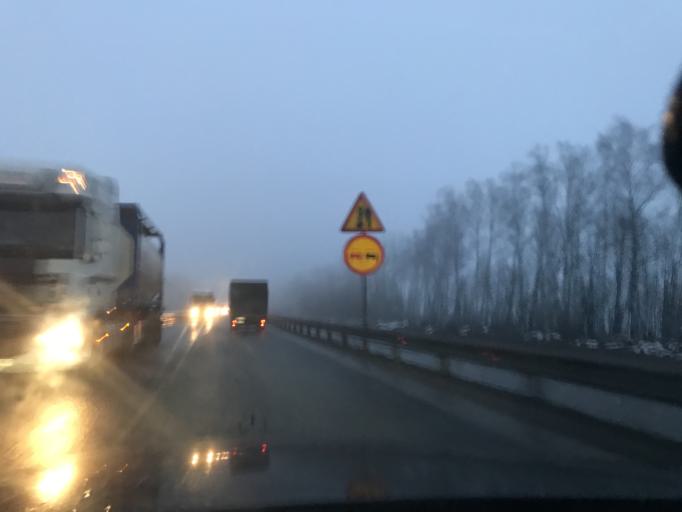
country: RU
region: Vladimir
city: Novovyazniki
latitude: 56.2116
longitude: 42.2647
